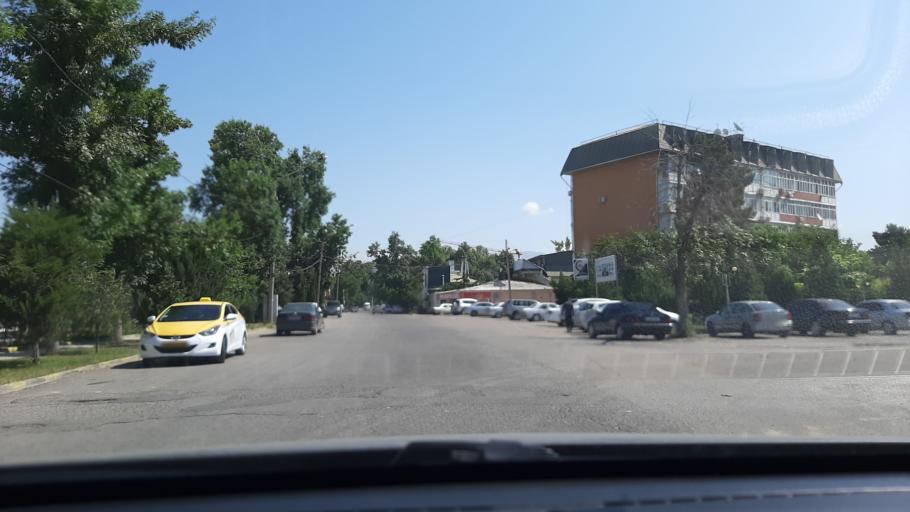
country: TJ
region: Dushanbe
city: Dushanbe
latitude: 38.5552
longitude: 68.7563
